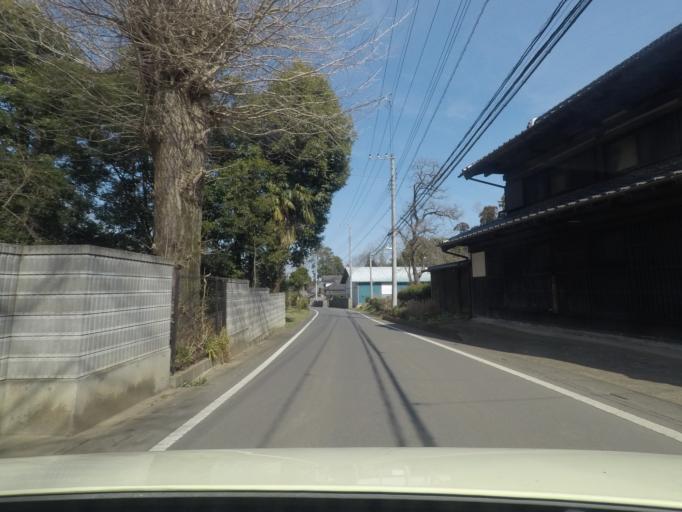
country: JP
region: Ibaraki
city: Okunoya
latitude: 36.2062
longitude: 140.4196
